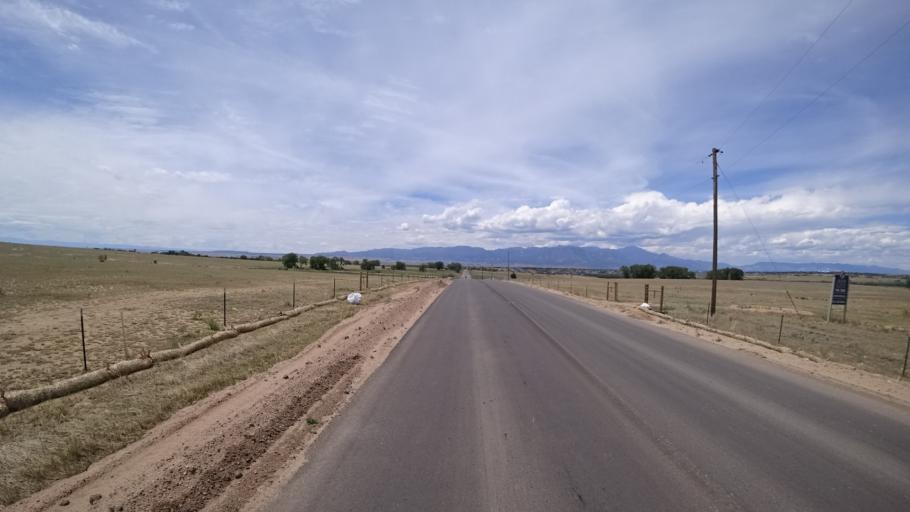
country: US
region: Colorado
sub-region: El Paso County
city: Fountain
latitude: 38.6940
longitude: -104.6501
